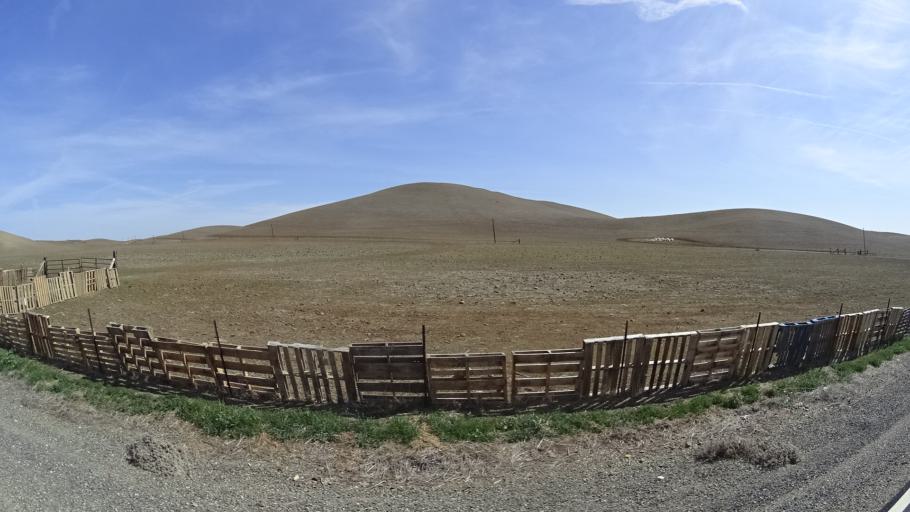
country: US
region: California
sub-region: Glenn County
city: Willows
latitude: 39.5414
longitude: -122.3458
